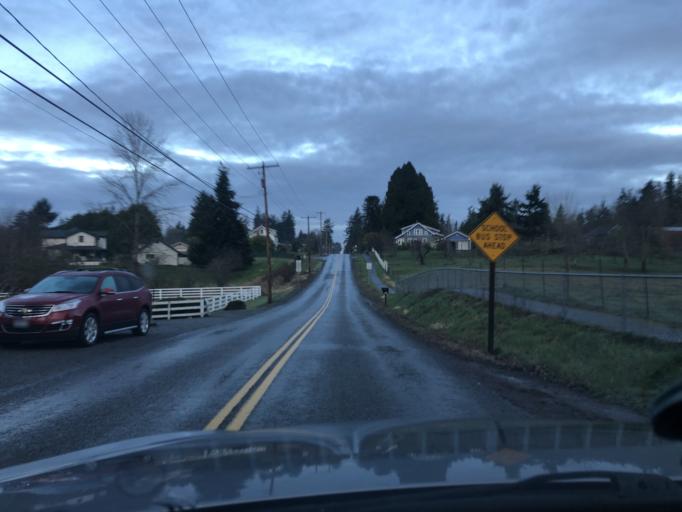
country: US
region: Washington
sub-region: Pierce County
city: North Puyallup
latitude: 47.2249
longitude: -122.2728
